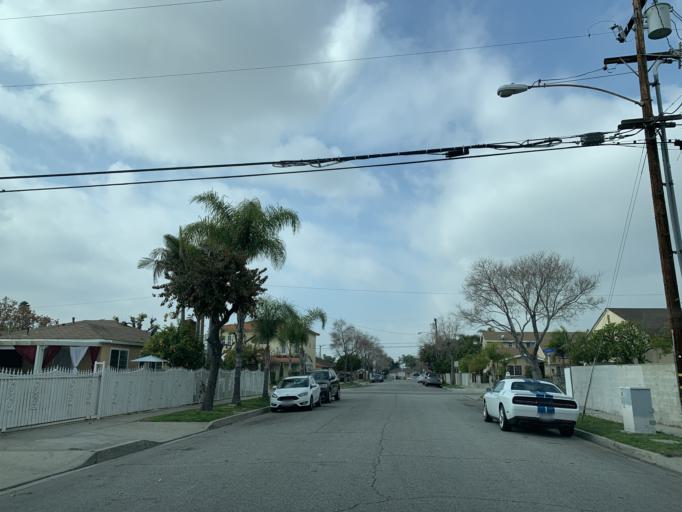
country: US
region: California
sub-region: Los Angeles County
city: Azusa
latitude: 34.1162
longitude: -117.9114
